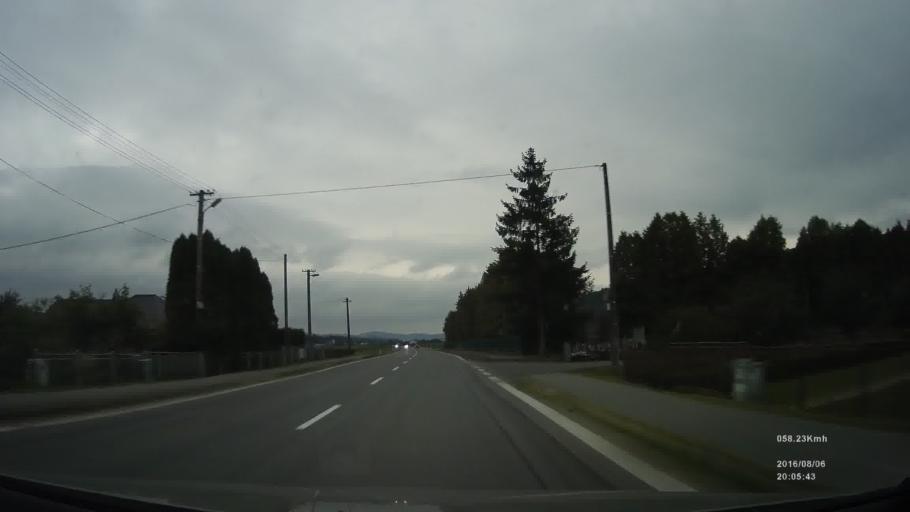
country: SK
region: Presovsky
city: Stropkov
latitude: 49.2330
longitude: 21.6274
